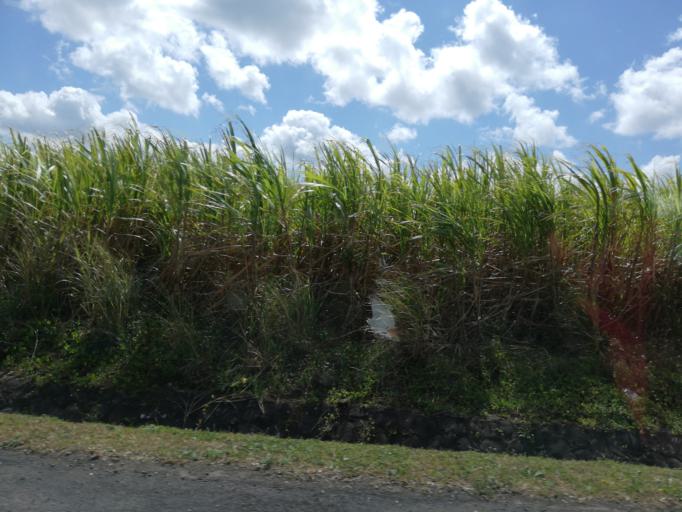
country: MU
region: Plaines Wilhems
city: Quatre Bornes
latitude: -20.2795
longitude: 57.5075
